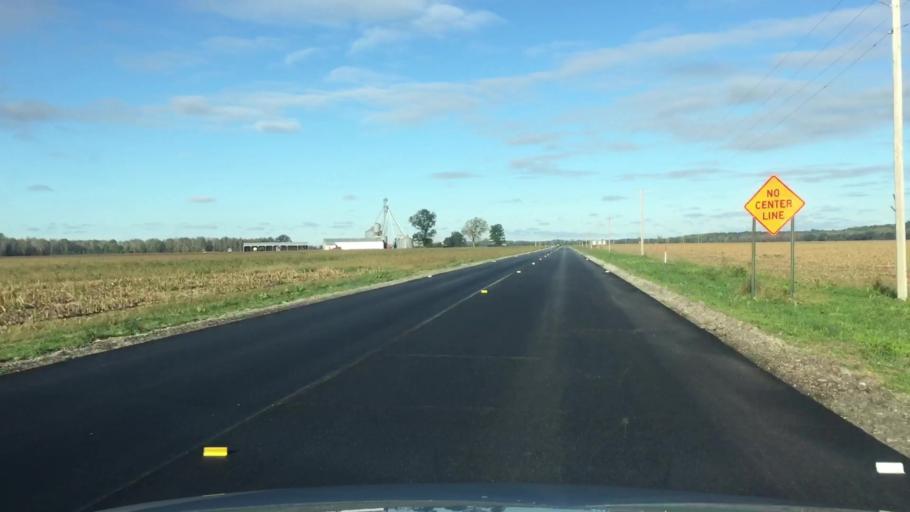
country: US
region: Missouri
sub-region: Howard County
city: New Franklin
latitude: 38.9960
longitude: -92.6632
